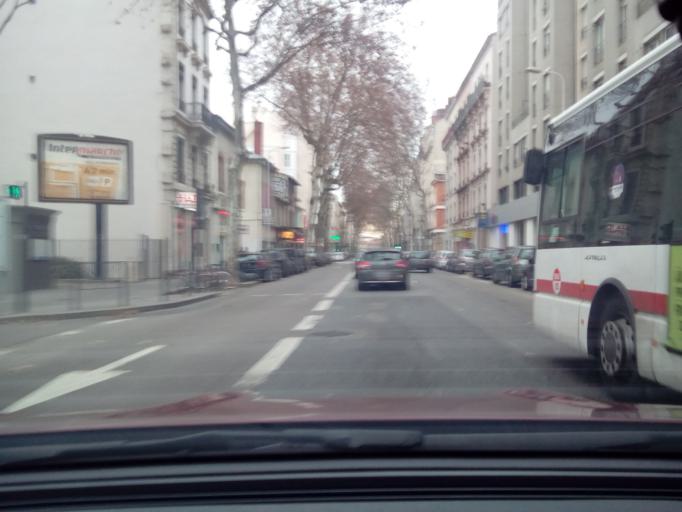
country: FR
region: Rhone-Alpes
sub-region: Departement du Rhone
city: Villeurbanne
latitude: 45.7637
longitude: 4.8655
